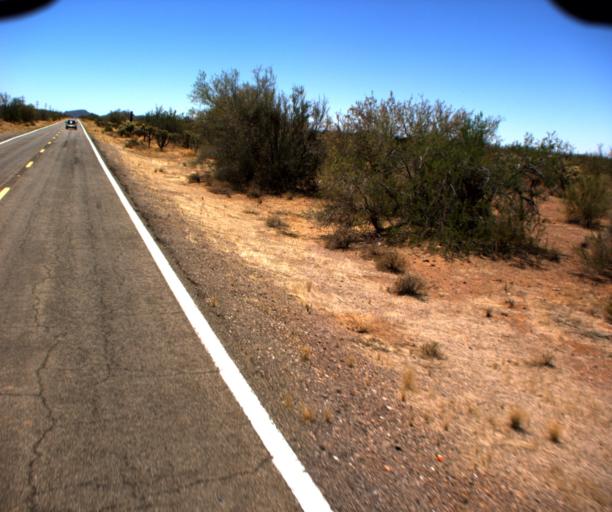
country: US
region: Arizona
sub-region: Pima County
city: Sells
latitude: 32.0330
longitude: -112.0117
